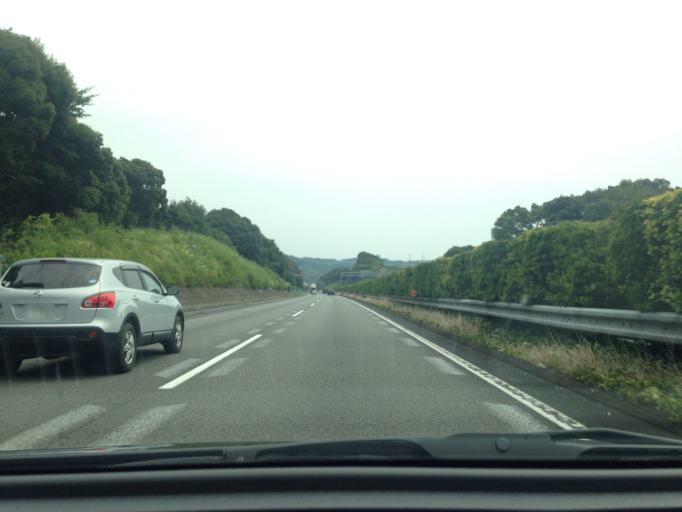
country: JP
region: Shizuoka
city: Shimada
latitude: 34.7553
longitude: 138.1882
